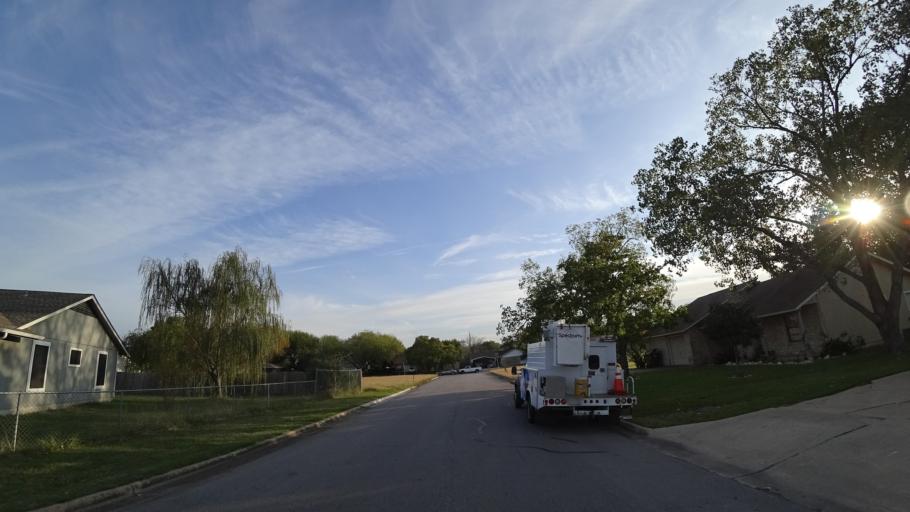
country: US
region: Texas
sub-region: Williamson County
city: Round Rock
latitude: 30.5030
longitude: -97.6737
